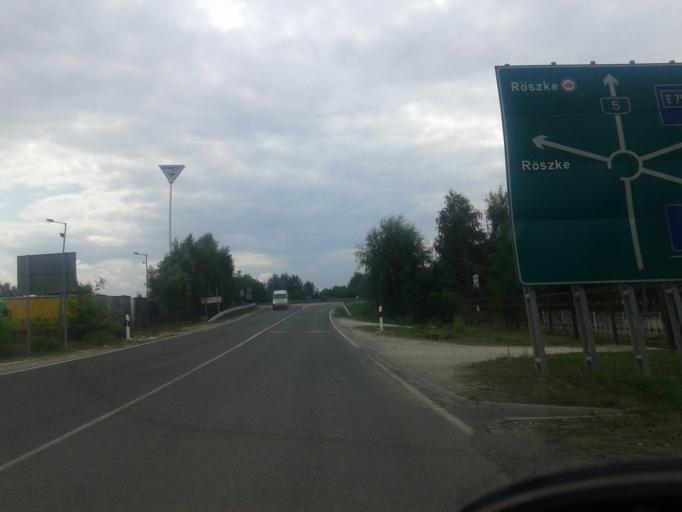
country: HU
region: Csongrad
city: Roszke
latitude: 46.1912
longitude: 20.0000
